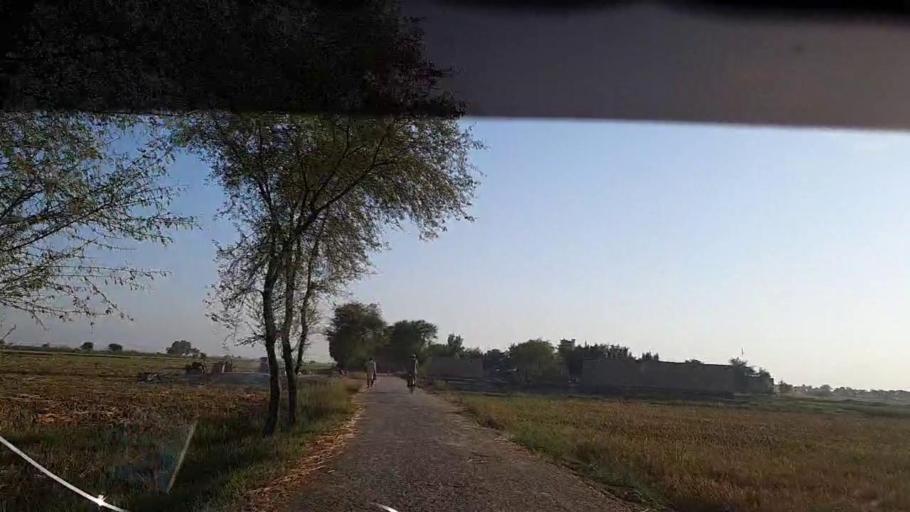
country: PK
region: Sindh
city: Ratodero
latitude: 27.8669
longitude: 68.2079
